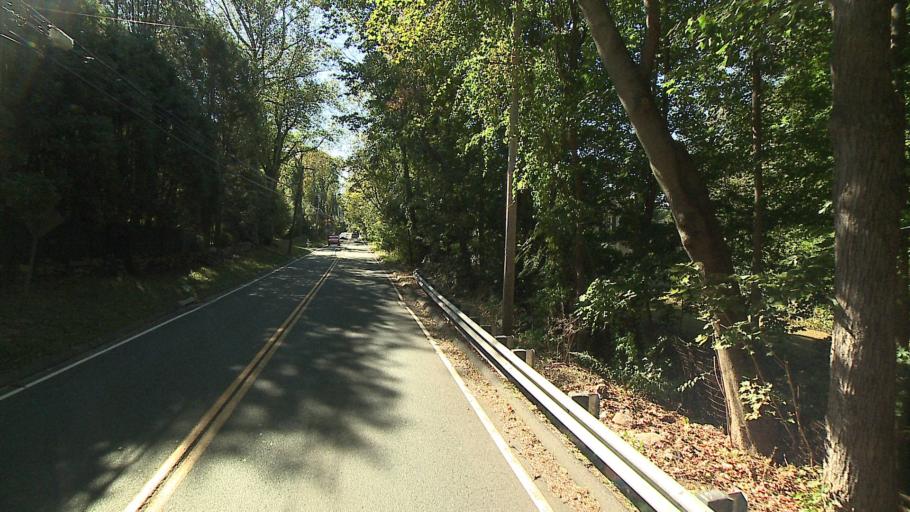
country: US
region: Connecticut
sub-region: Fairfield County
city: Darien
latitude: 41.1102
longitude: -73.4858
